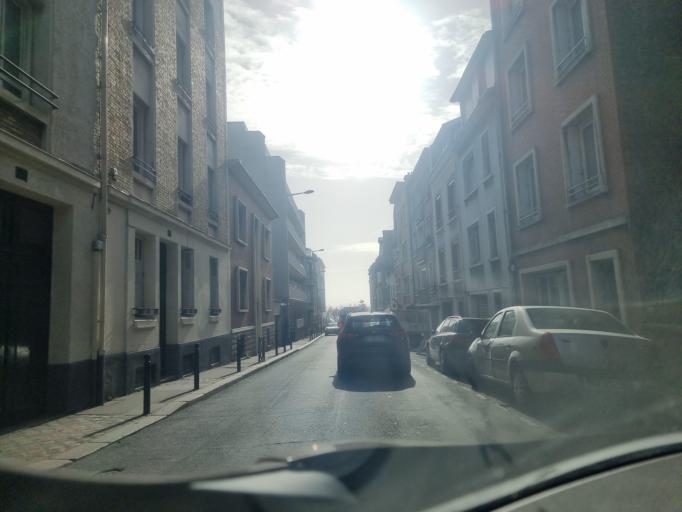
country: FR
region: Haute-Normandie
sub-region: Departement de la Seine-Maritime
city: Le Havre
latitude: 49.4969
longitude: 0.0941
